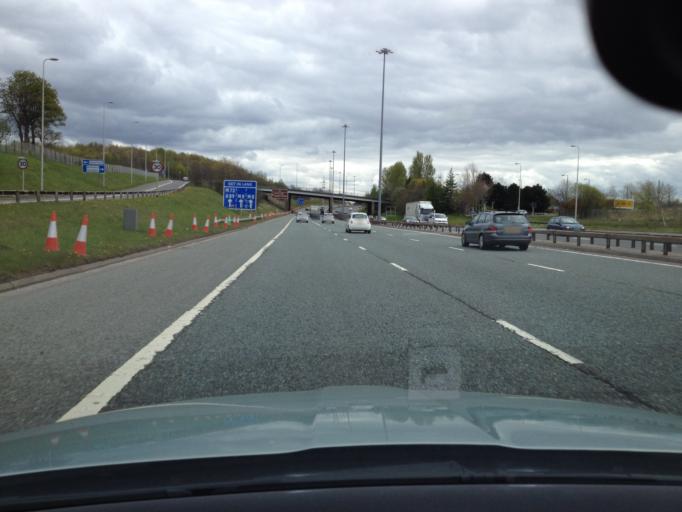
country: GB
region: Scotland
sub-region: North Lanarkshire
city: Chryston
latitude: 55.8623
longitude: -4.1128
